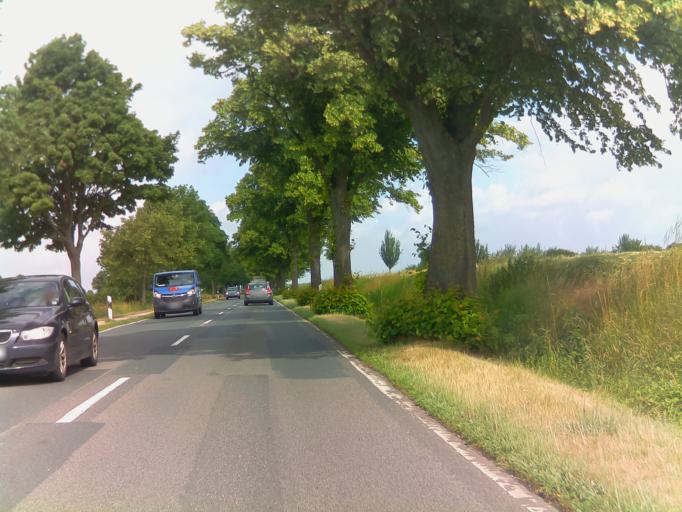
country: DE
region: Lower Saxony
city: Ronnenberg
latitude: 52.2401
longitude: 9.6477
